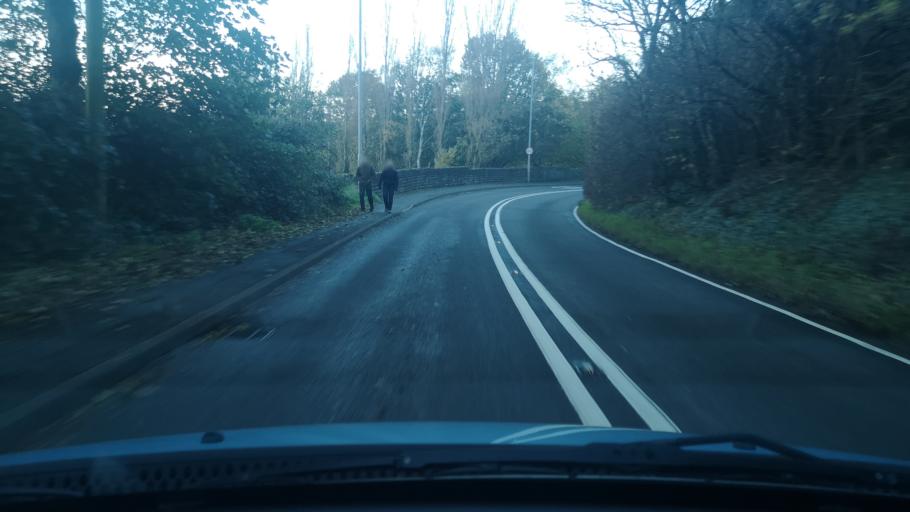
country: GB
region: England
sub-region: City and Borough of Wakefield
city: Middlestown
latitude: 53.6375
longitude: -1.5854
